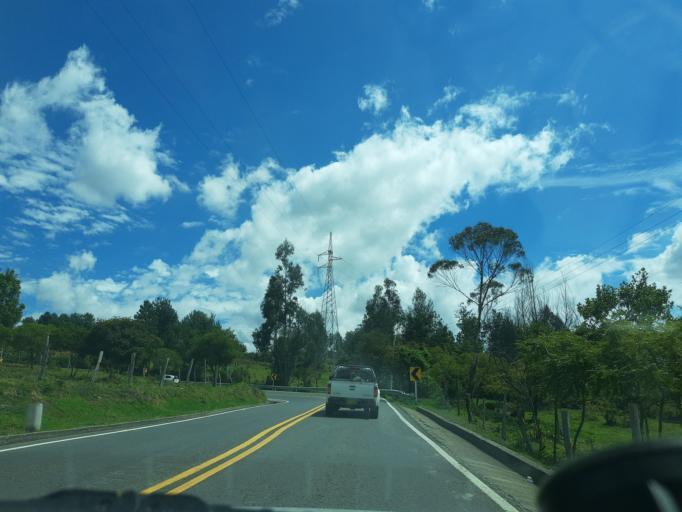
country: CO
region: Boyaca
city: Raquira
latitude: 5.5807
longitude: -73.6854
